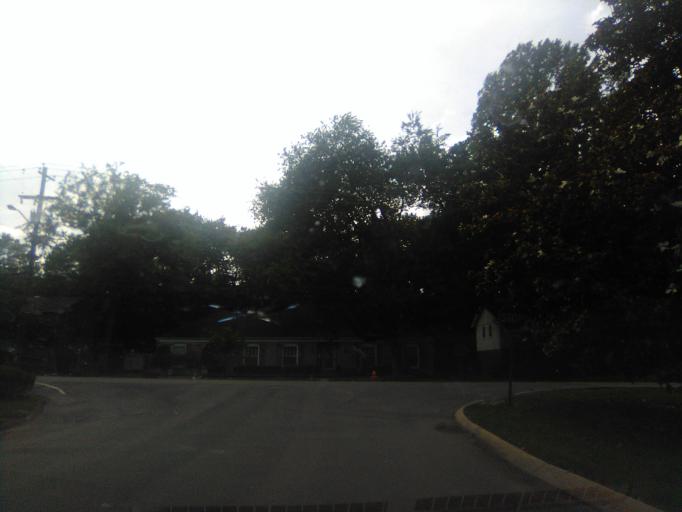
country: US
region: Tennessee
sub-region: Davidson County
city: Belle Meade
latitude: 36.0815
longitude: -86.8852
